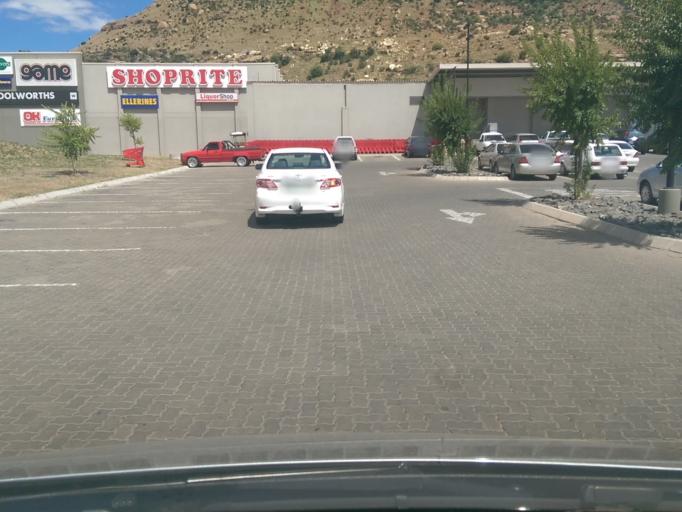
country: LS
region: Maseru
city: Maseru
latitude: -29.3349
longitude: 27.4854
